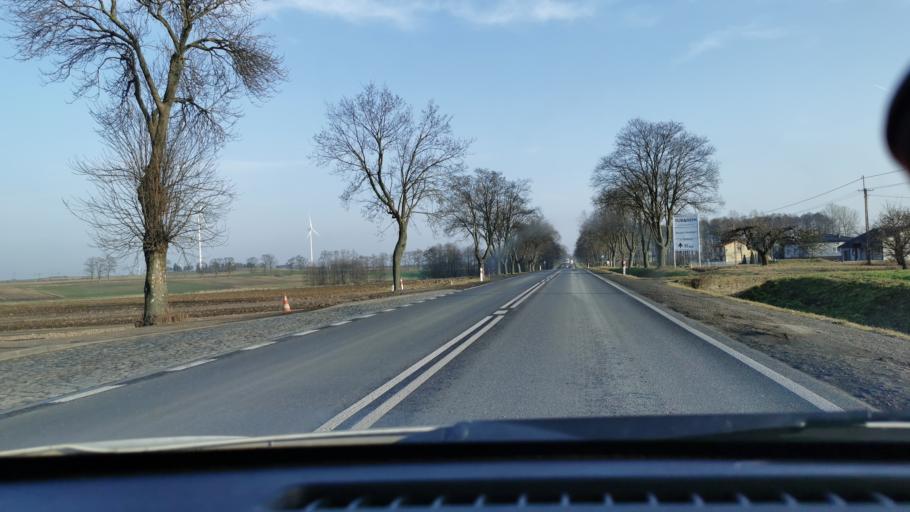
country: PL
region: Lodz Voivodeship
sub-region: Powiat sieradzki
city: Blaszki
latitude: 51.6367
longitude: 18.5227
